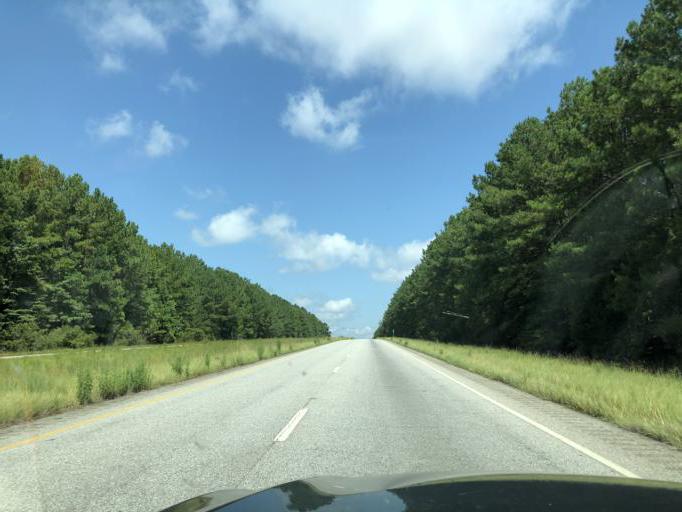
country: US
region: Alabama
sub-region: Henry County
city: Abbeville
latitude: 31.6831
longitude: -85.2790
